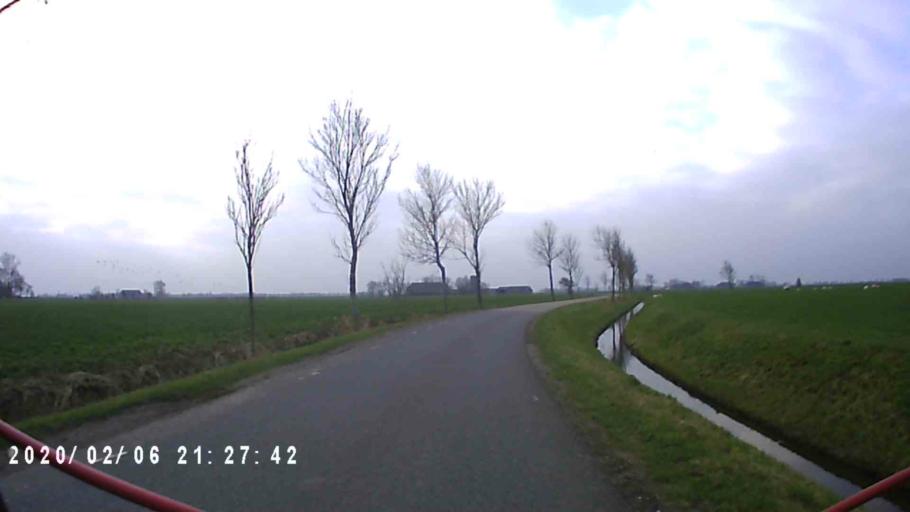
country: NL
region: Groningen
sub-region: Gemeente Zuidhorn
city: Oldehove
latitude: 53.2831
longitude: 6.3780
